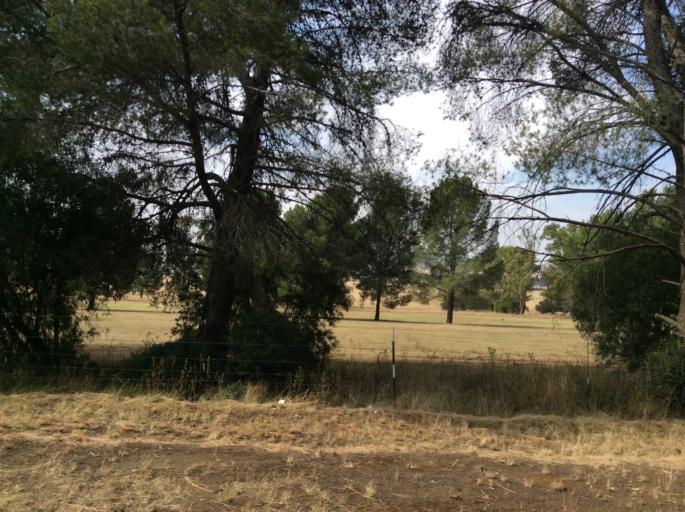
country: ZA
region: Orange Free State
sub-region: Xhariep District Municipality
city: Dewetsdorp
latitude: -29.5707
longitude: 26.6657
